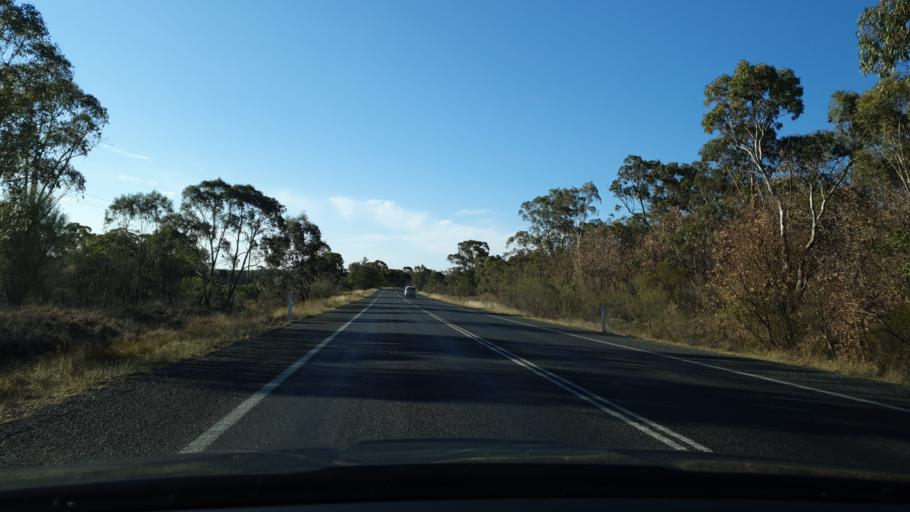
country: AU
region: Queensland
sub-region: Southern Downs
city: Stanthorpe
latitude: -28.6721
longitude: 151.9188
